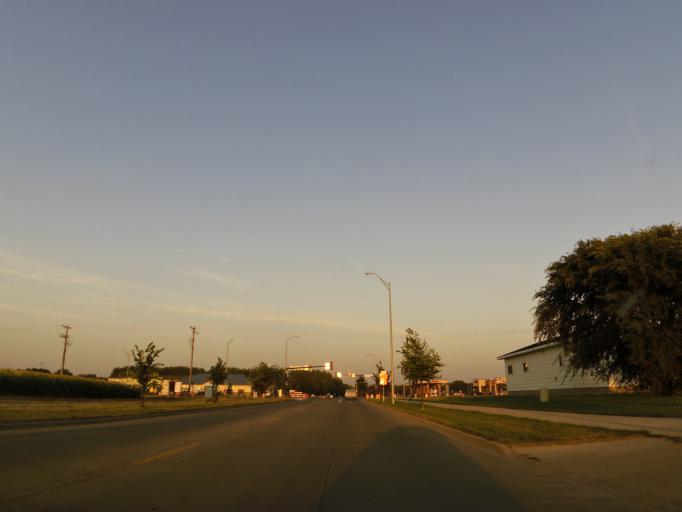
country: US
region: North Dakota
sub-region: Grand Forks County
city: Grand Forks
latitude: 47.8823
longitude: -97.0470
